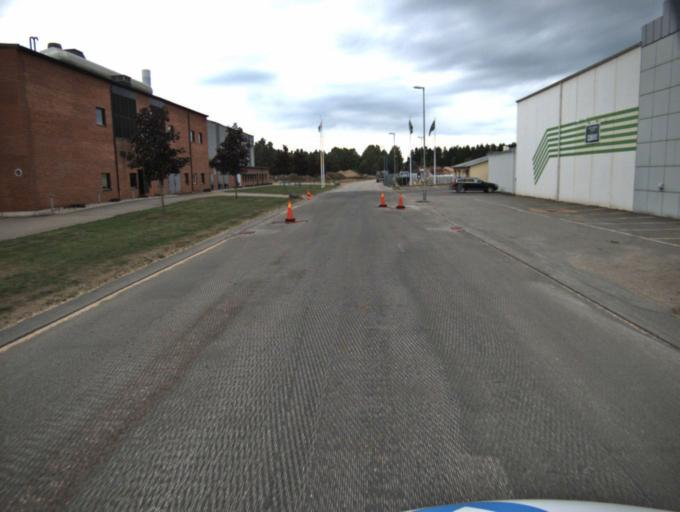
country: SE
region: Vaestra Goetaland
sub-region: Ulricehamns Kommun
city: Ulricehamn
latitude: 57.8266
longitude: 13.4205
